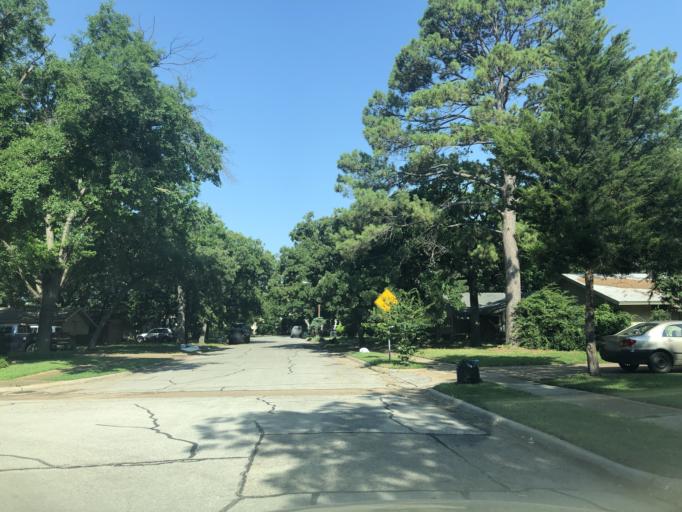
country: US
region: Texas
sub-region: Dallas County
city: Irving
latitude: 32.8040
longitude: -96.9740
